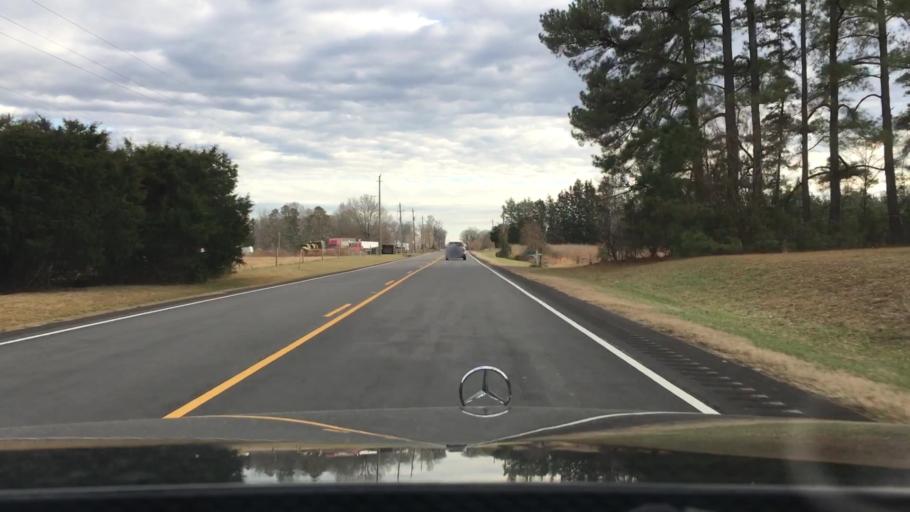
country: US
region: North Carolina
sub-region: Caswell County
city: Yanceyville
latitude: 36.3814
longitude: -79.2651
